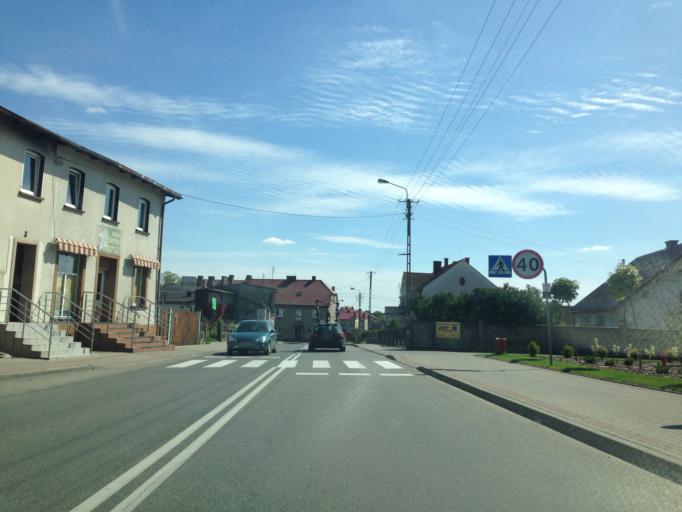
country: PL
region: Kujawsko-Pomorskie
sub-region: Powiat swiecki
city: Osie
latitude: 53.5994
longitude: 18.3436
